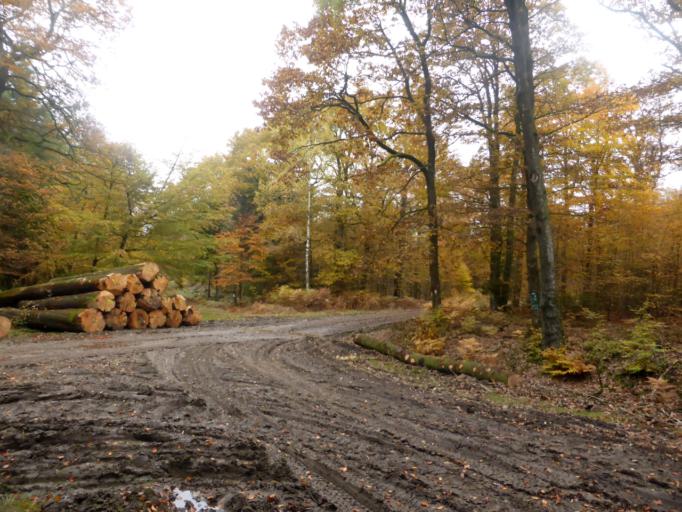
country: BE
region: Wallonia
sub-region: Province du Luxembourg
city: Herbeumont
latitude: 49.7463
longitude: 5.2029
